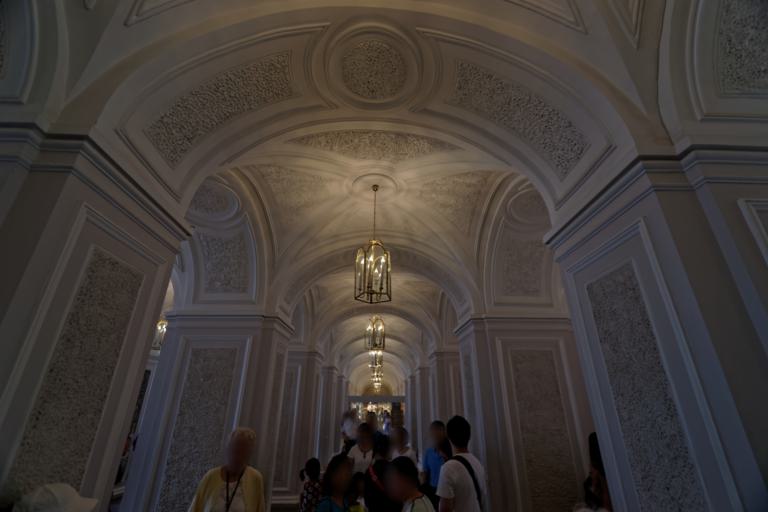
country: RU
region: St.-Petersburg
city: Pushkin
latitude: 59.7160
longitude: 30.3957
